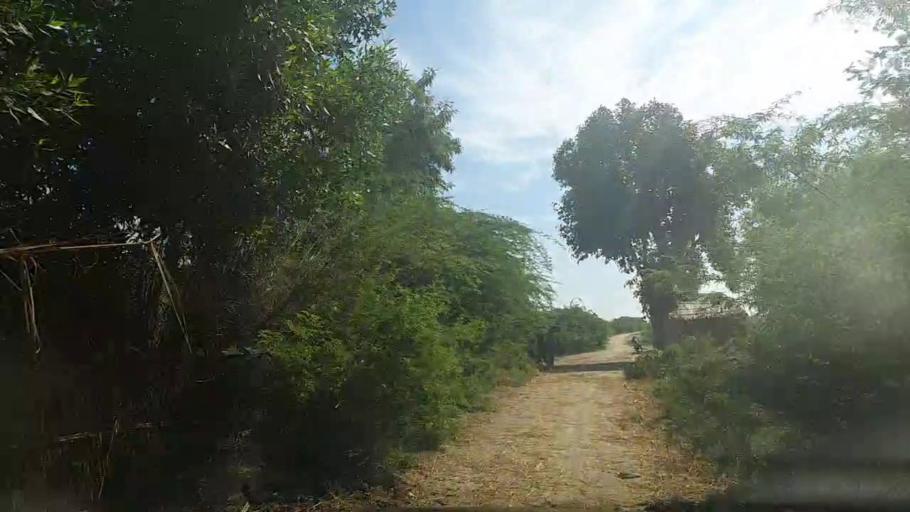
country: PK
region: Sindh
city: Mirpur Batoro
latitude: 24.6634
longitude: 68.1880
